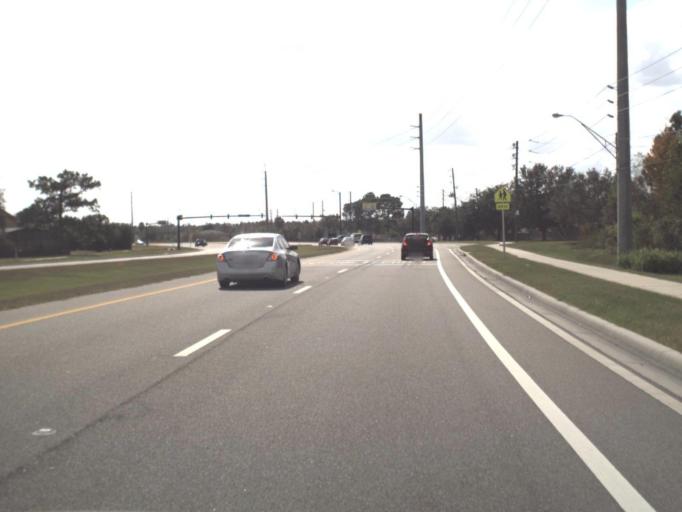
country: US
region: Florida
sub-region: Osceola County
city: Campbell
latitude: 28.2316
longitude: -81.4875
